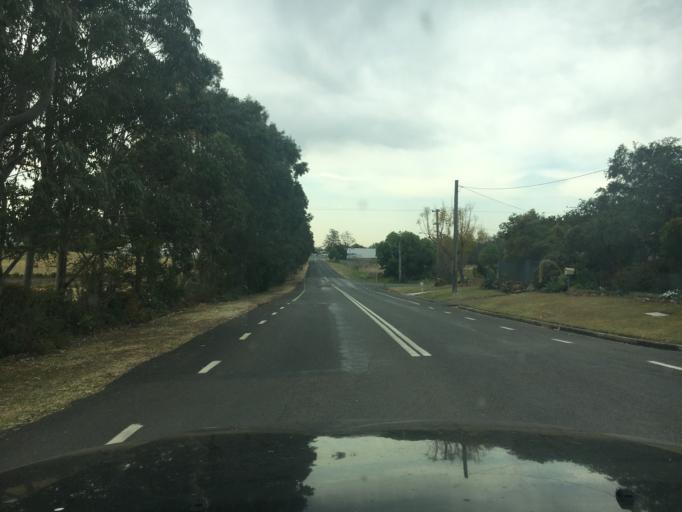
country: AU
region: New South Wales
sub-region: Maitland Municipality
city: East Maitland
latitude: -32.7503
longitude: 151.5758
